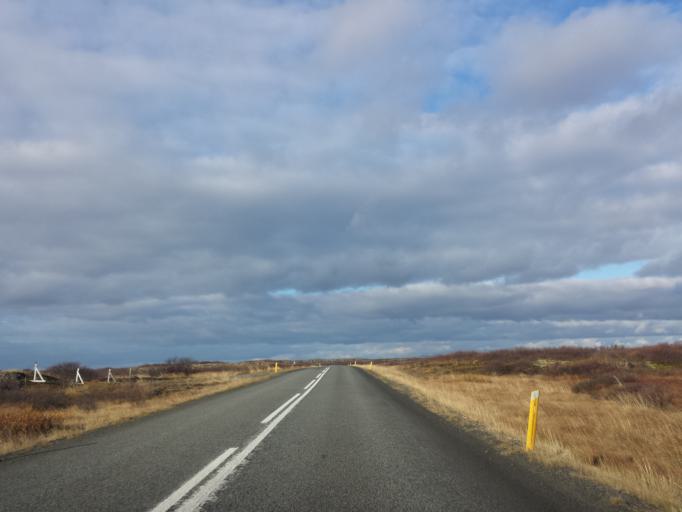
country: IS
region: West
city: Borgarnes
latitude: 64.5980
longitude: -22.0145
